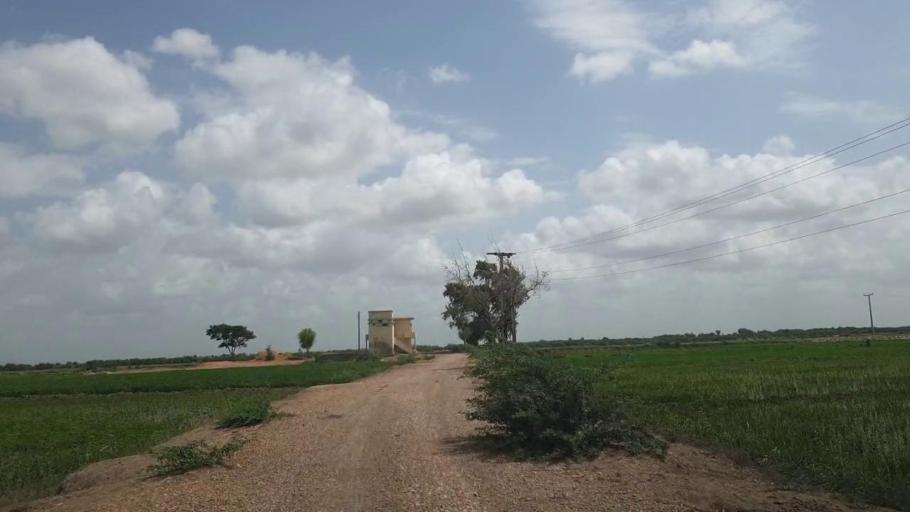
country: PK
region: Sindh
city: Tando Bago
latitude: 24.6473
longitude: 68.9938
